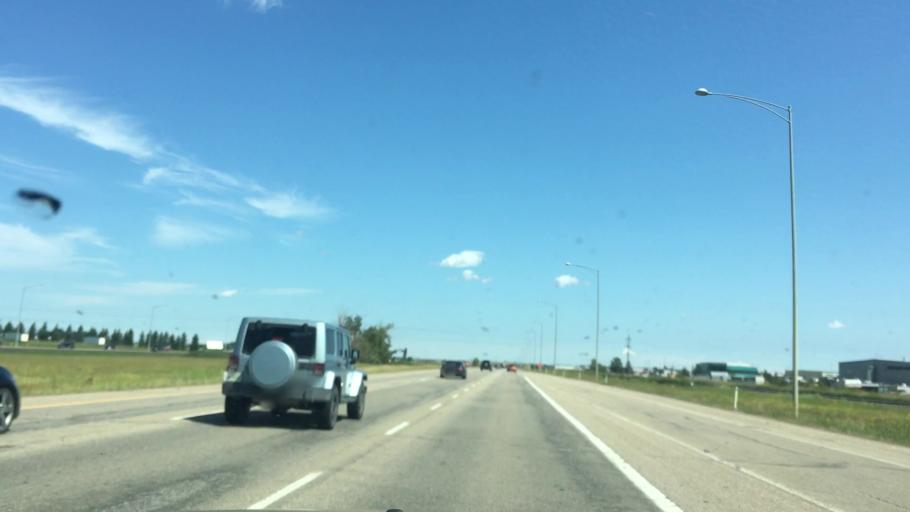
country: CA
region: Alberta
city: Leduc
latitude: 53.3639
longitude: -113.5310
